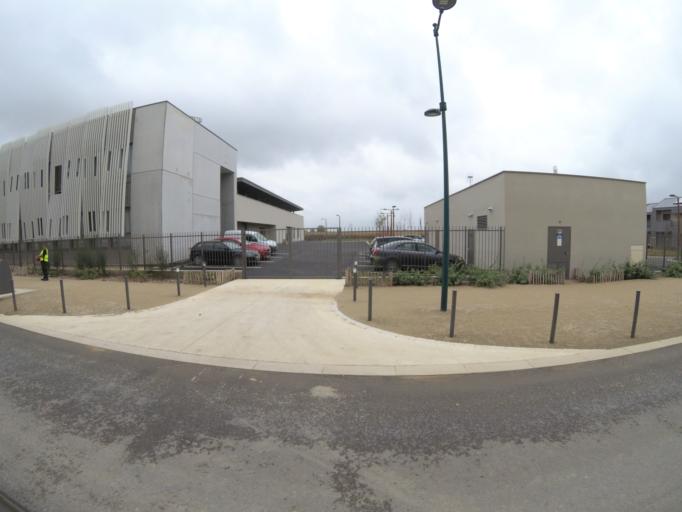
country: FR
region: Ile-de-France
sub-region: Departement de Seine-et-Marne
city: Montevrain
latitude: 48.8610
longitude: 2.7597
